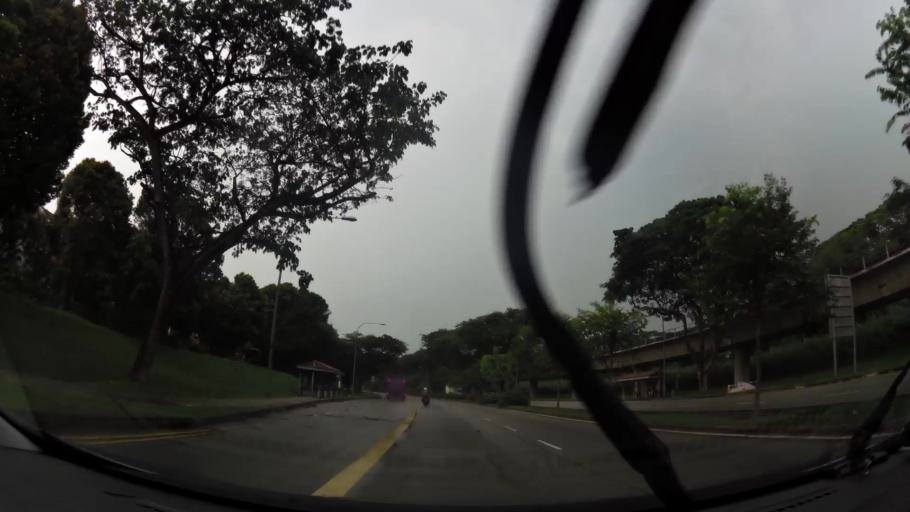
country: MY
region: Johor
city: Kampung Pasir Gudang Baru
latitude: 1.3891
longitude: 103.8410
